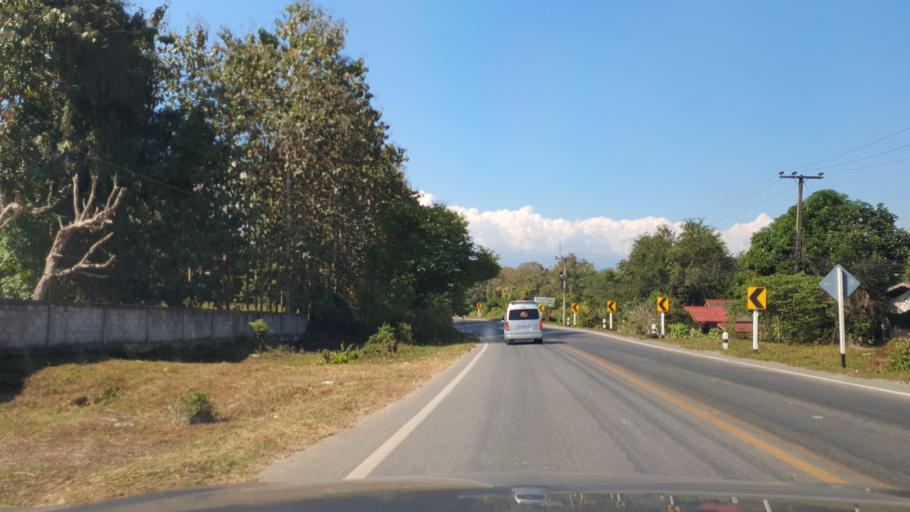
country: TH
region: Nan
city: Tha Wang Pha
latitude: 19.1048
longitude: 100.8185
